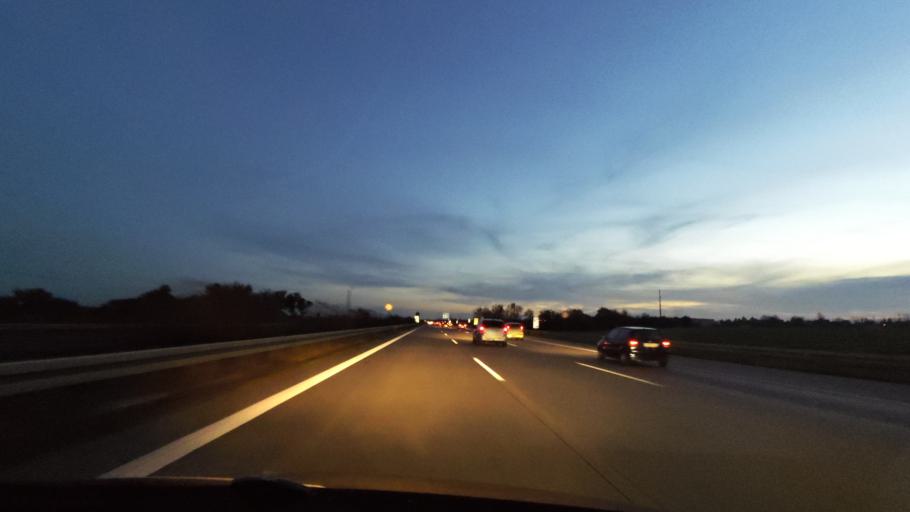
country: DE
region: Saxony-Anhalt
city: Osterfeld
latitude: 51.0996
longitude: 11.9557
